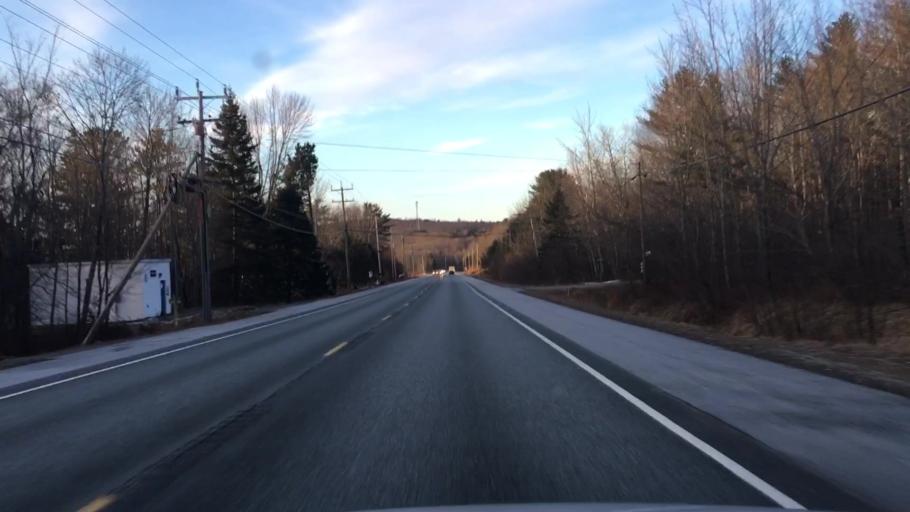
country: US
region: Maine
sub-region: Hancock County
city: Dedham
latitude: 44.7085
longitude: -68.6016
